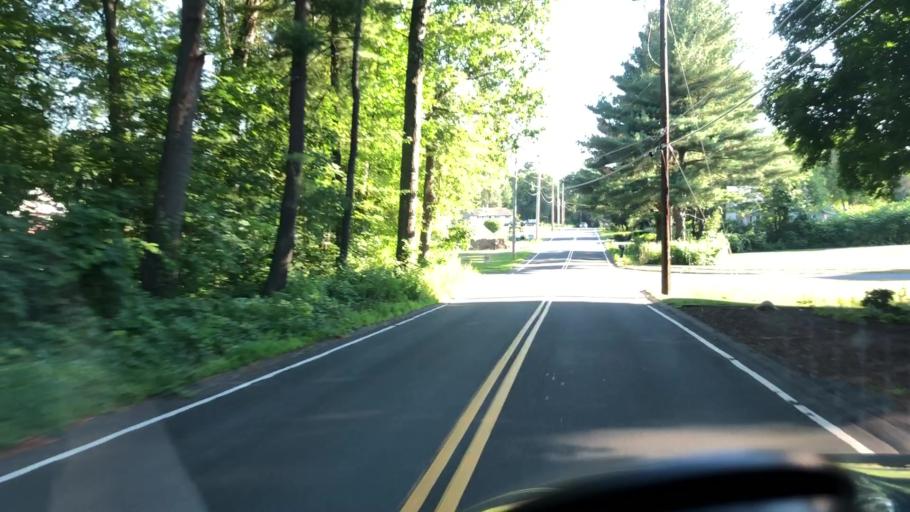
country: US
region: Massachusetts
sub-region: Hampshire County
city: Easthampton
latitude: 42.2467
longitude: -72.6553
